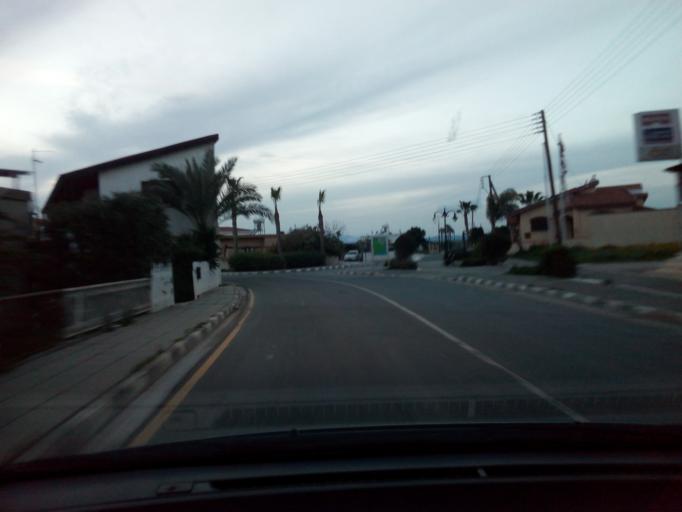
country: CY
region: Larnaka
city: Tersefanou
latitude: 34.8045
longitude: 33.4863
